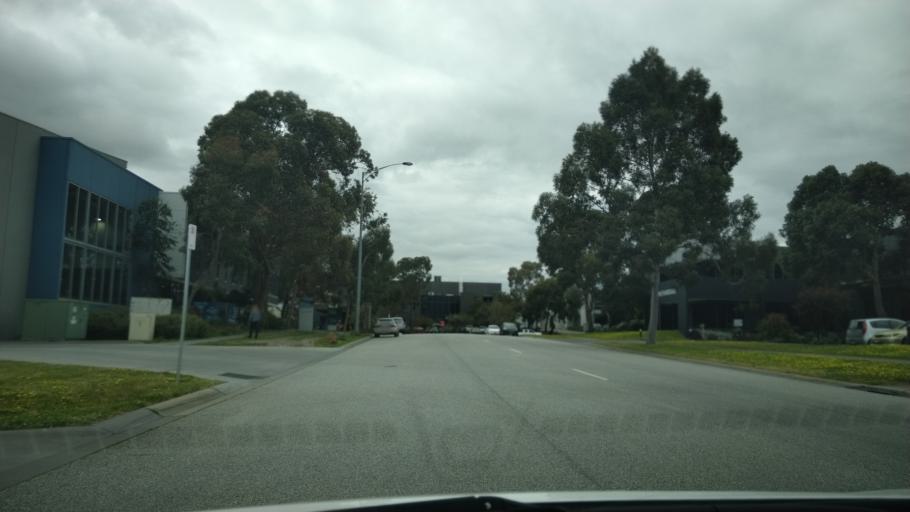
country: AU
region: Victoria
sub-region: Monash
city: Oakleigh South
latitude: -37.9483
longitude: 145.0813
